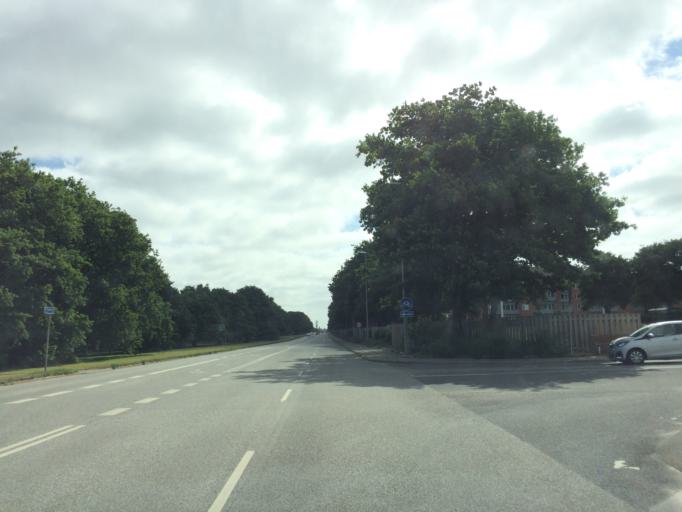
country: DK
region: Central Jutland
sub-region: Herning Kommune
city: Herning
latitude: 56.1453
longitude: 8.9531
